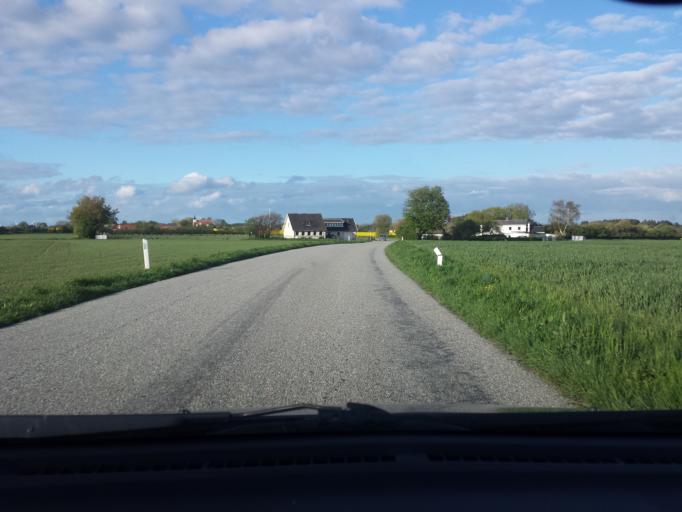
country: DK
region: South Denmark
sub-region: Langeland Kommune
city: Rudkobing
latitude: 54.8954
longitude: 10.7535
